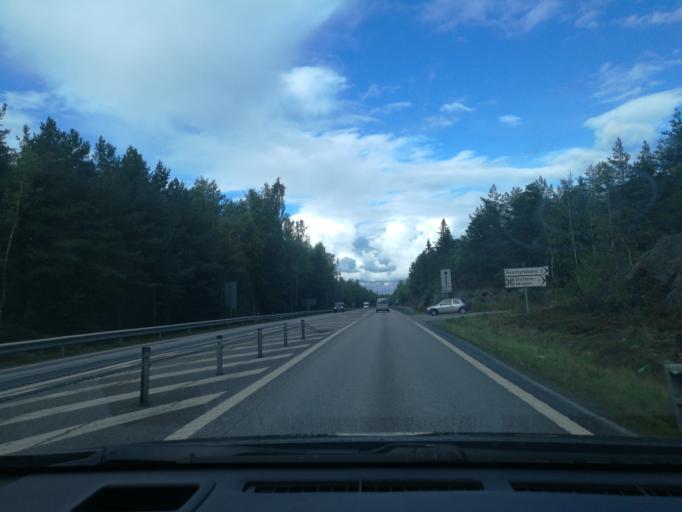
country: SE
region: OEstergoetland
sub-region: Norrkopings Kommun
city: Jursla
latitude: 58.7104
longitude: 16.1609
